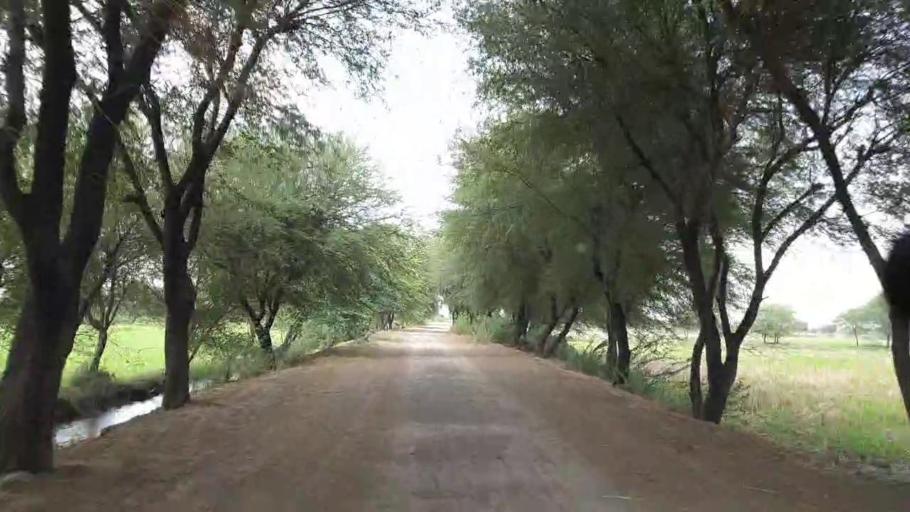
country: PK
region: Sindh
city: Tando Ghulam Ali
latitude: 25.0767
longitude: 68.8110
